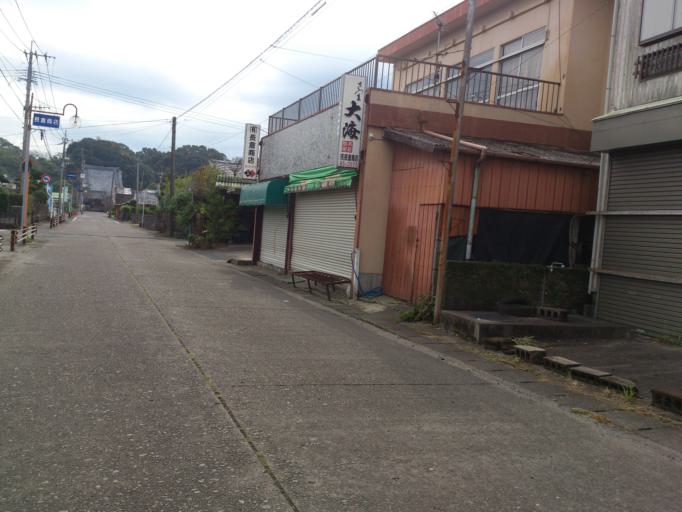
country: JP
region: Kagoshima
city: Kanoya
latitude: 31.3472
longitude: 130.9512
